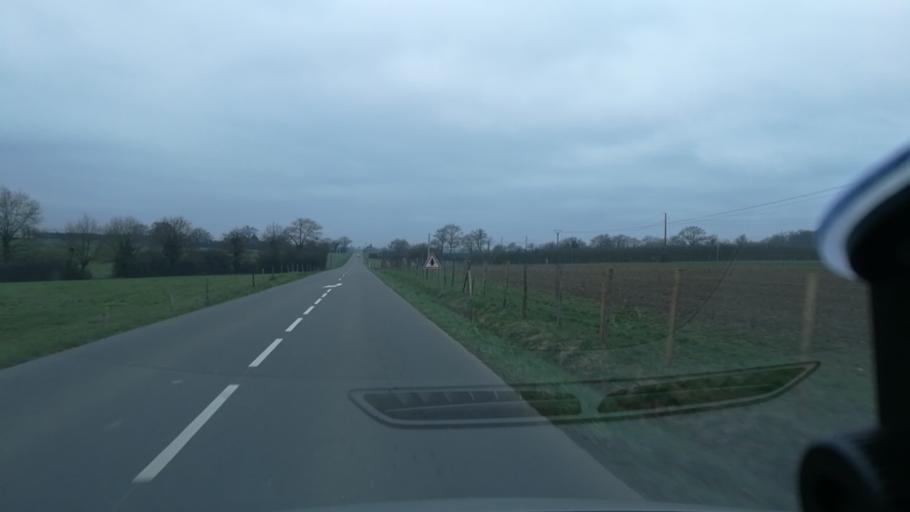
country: FR
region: Brittany
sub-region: Departement d'Ille-et-Vilaine
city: Coesmes
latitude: 47.8847
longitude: -1.4800
